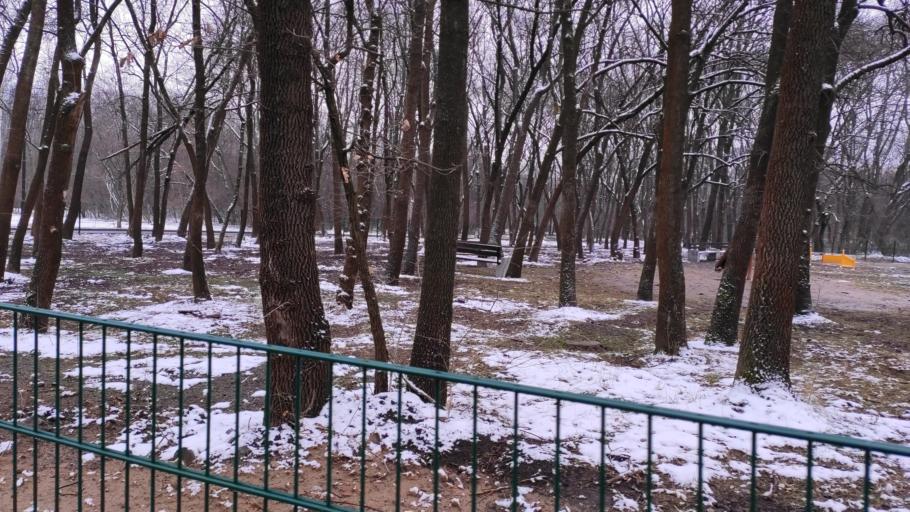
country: BG
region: Sofia-Capital
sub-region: Stolichna Obshtina
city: Sofia
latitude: 42.7104
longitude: 23.2788
